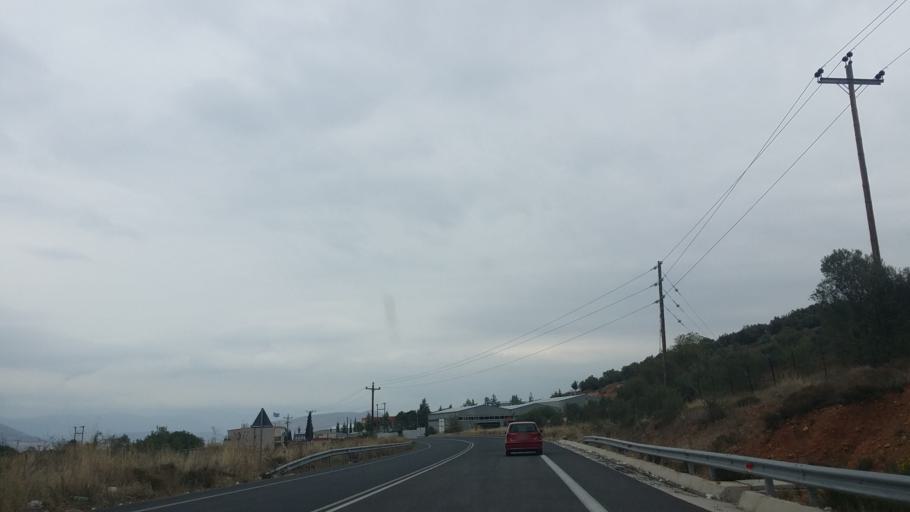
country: GR
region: Central Greece
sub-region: Nomos Voiotias
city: Thivai
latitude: 38.3201
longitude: 23.2702
